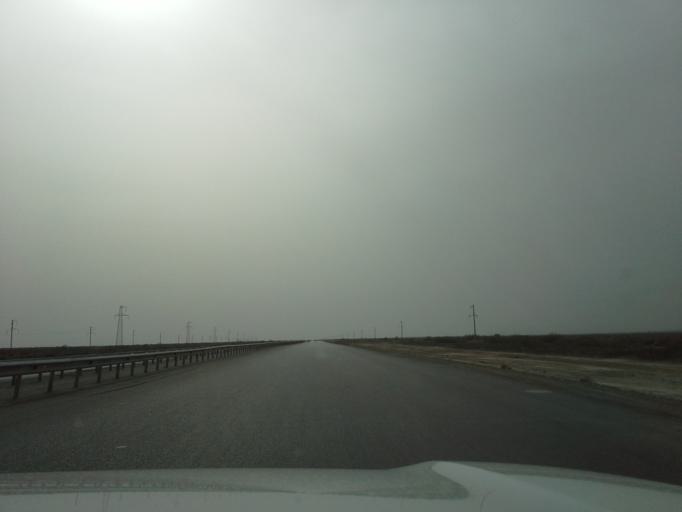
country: TM
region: Ahal
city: Kaka
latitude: 37.5147
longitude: 59.4366
